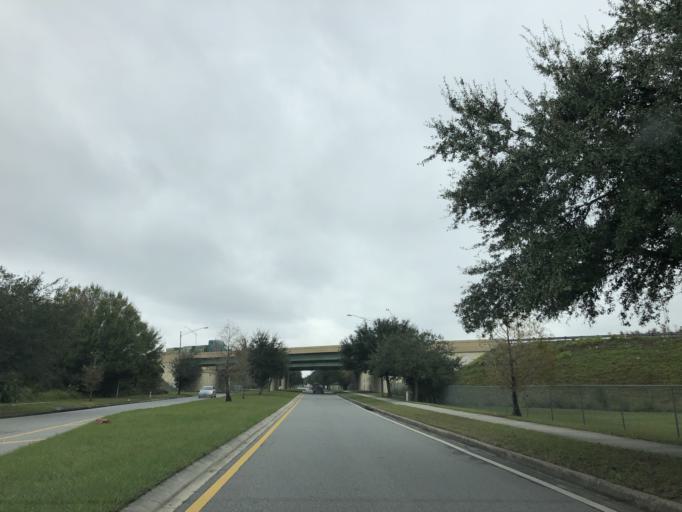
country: US
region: Florida
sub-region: Orange County
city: Hunters Creek
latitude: 28.3696
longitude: -81.3994
